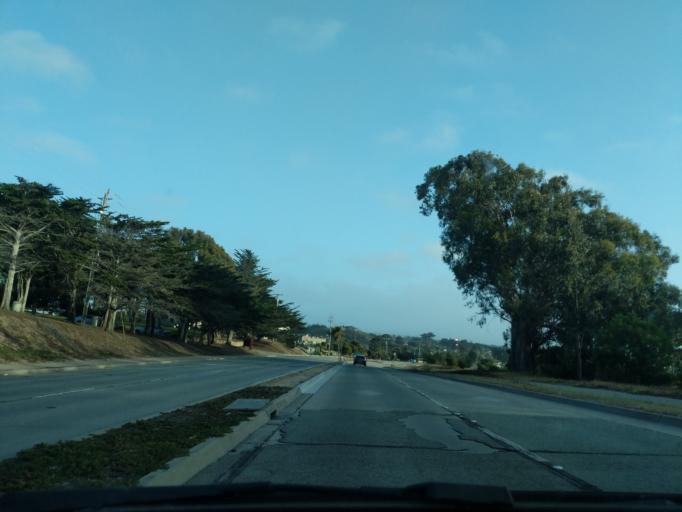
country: US
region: California
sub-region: Monterey County
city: Marina
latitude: 36.6915
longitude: -121.7983
